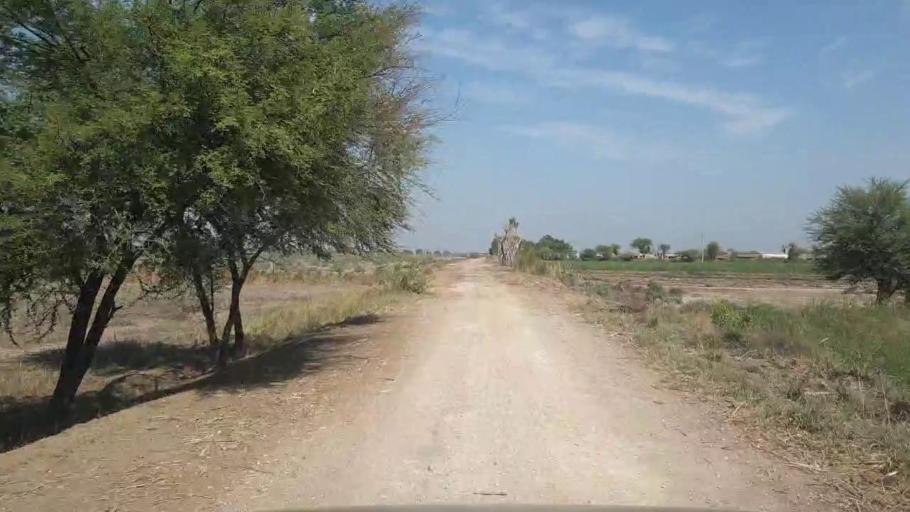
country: PK
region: Sindh
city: Mirwah Gorchani
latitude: 25.4368
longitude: 69.1882
